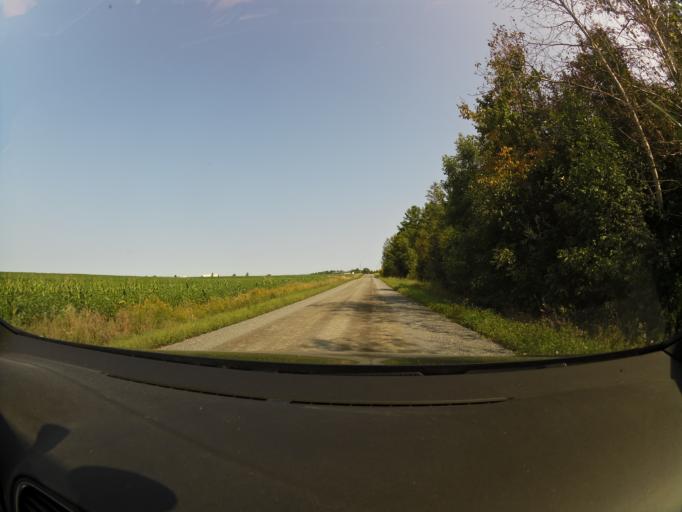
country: CA
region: Ontario
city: Arnprior
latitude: 45.4300
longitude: -76.1984
